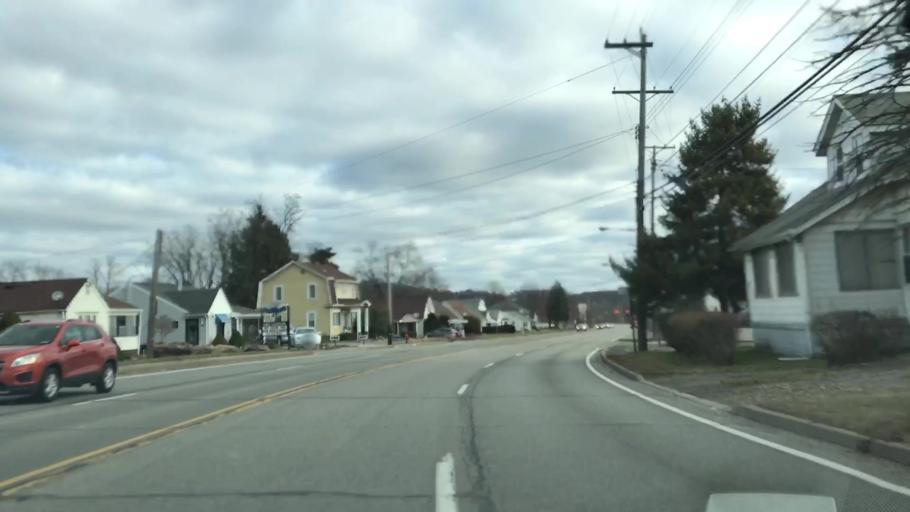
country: US
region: Pennsylvania
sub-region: Beaver County
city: Aliquippa
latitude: 40.6067
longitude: -80.2863
